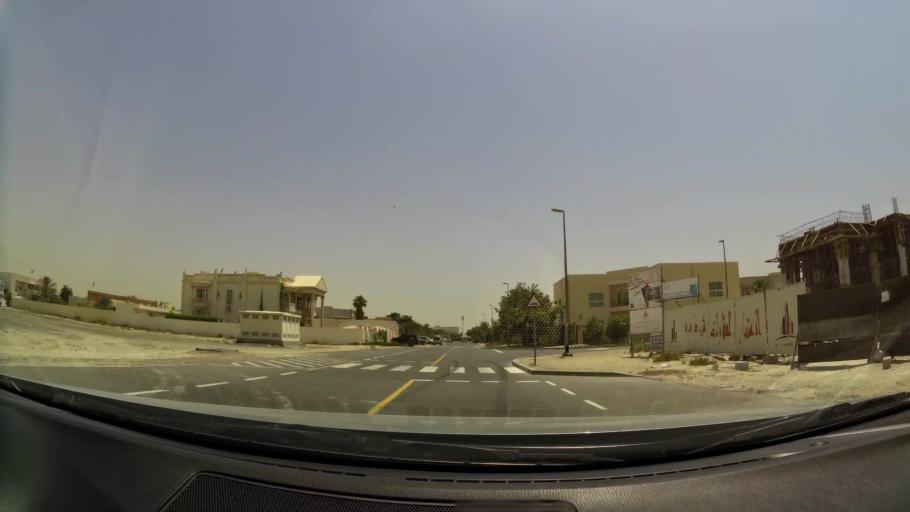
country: AE
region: Dubai
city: Dubai
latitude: 25.0955
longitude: 55.2085
